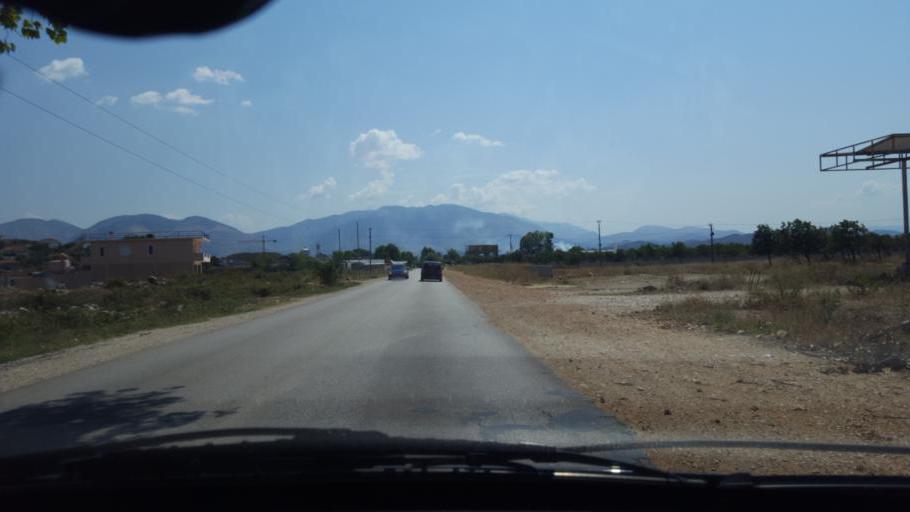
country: AL
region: Vlore
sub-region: Rrethi i Delvines
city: Finiq
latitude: 39.8791
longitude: 20.0448
